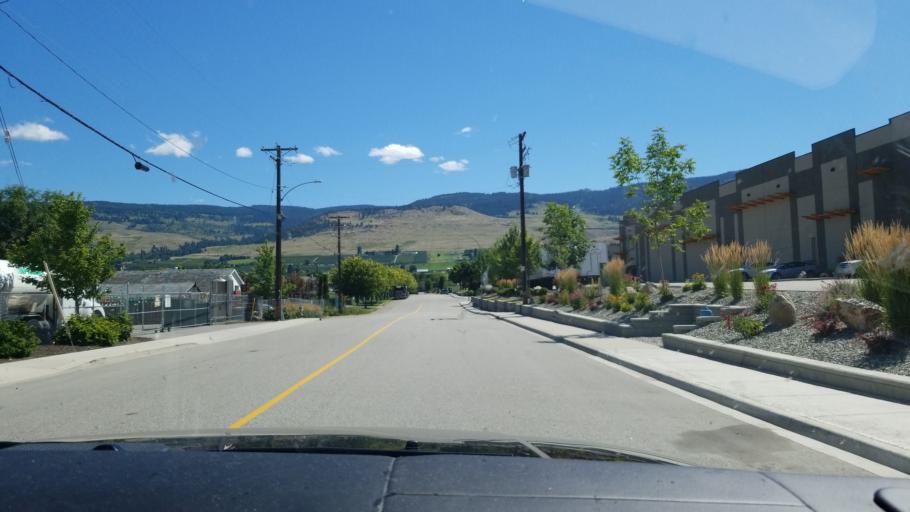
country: CA
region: British Columbia
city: Kelowna
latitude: 49.9218
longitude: -119.3830
